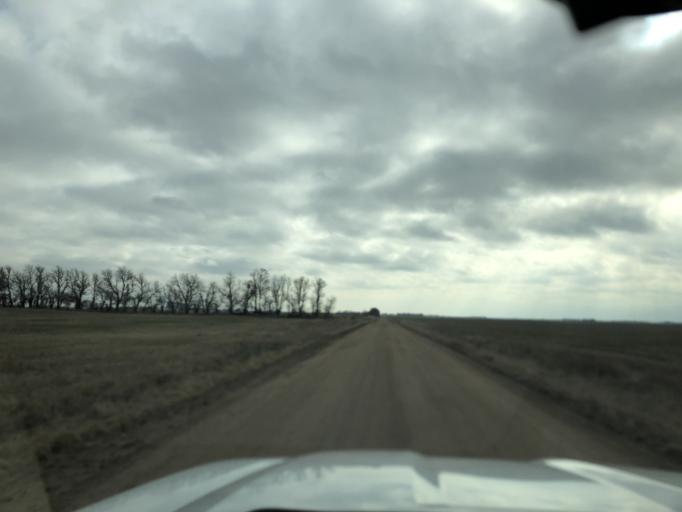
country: US
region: Kansas
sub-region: Reno County
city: Nickerson
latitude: 37.9940
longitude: -98.2158
